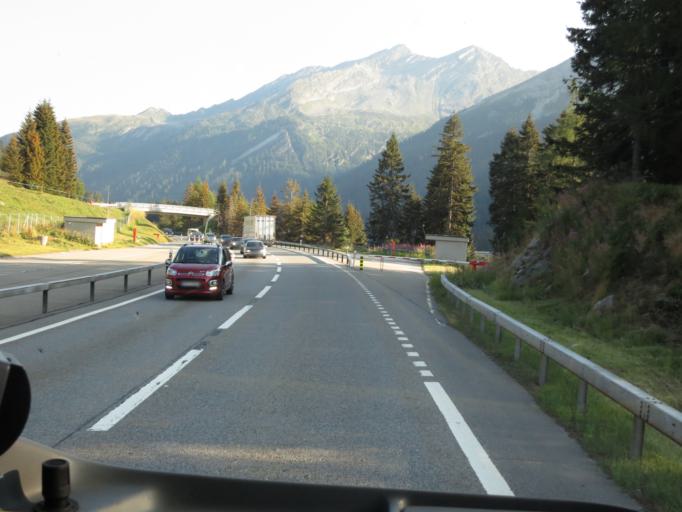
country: CH
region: Grisons
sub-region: Moesa District
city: Mesocco
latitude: 46.4514
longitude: 9.1903
